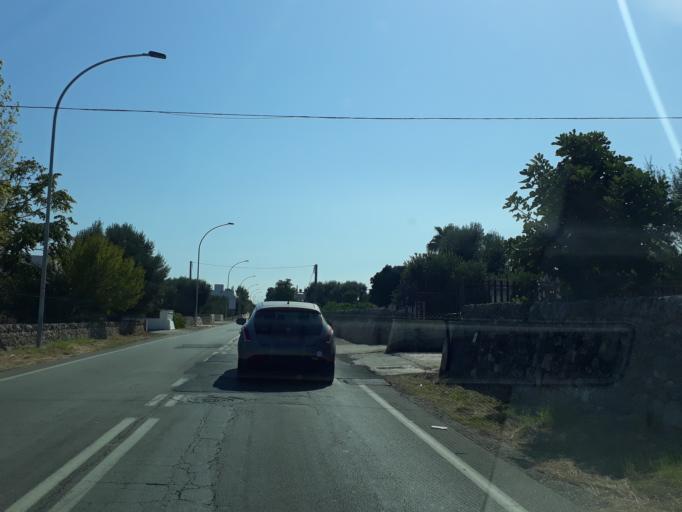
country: IT
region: Apulia
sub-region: Provincia di Bari
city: Monopoli
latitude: 40.9340
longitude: 17.3102
